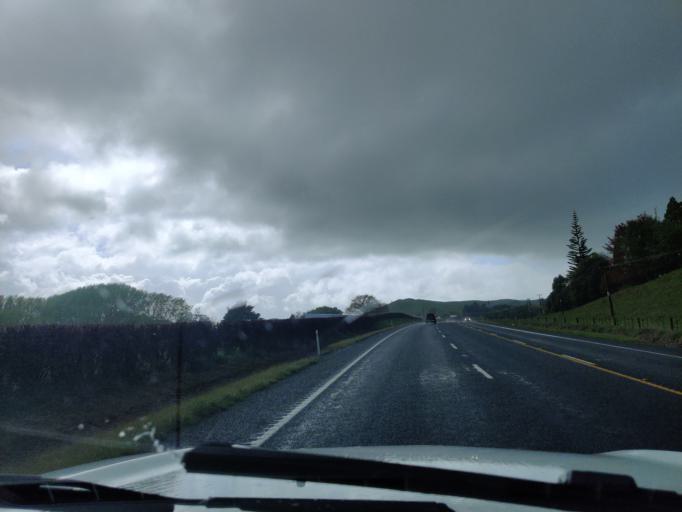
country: NZ
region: Waikato
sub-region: Matamata-Piako District
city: Matamata
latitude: -37.9855
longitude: 175.7205
